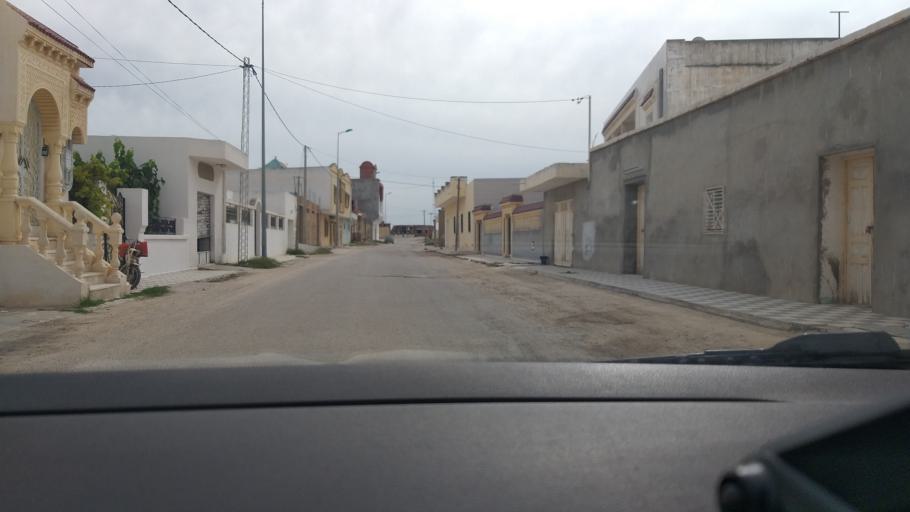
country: TN
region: Al Mahdiyah
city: El Jem
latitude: 35.2849
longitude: 10.7114
